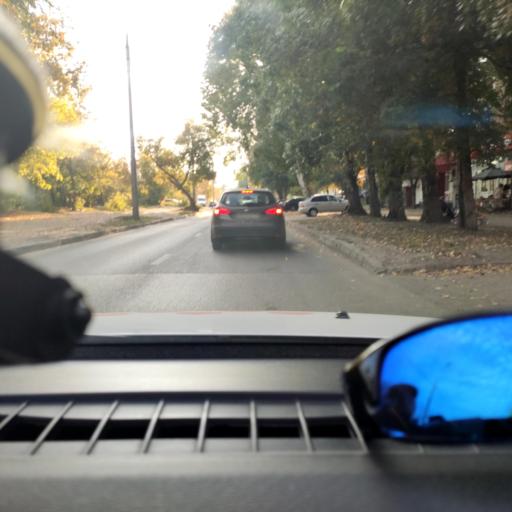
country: RU
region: Samara
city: Samara
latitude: 53.2327
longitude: 50.2275
